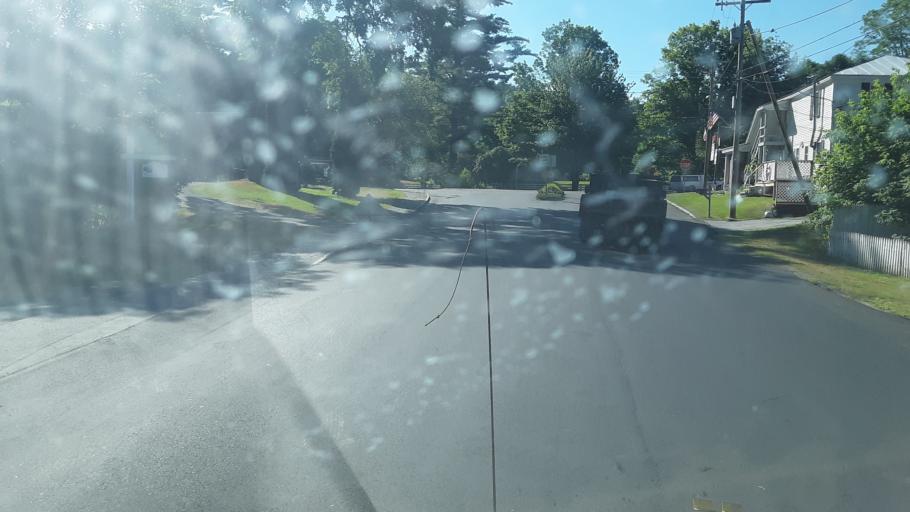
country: US
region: New Hampshire
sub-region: Grafton County
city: Orford
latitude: 43.9057
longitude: -72.1378
